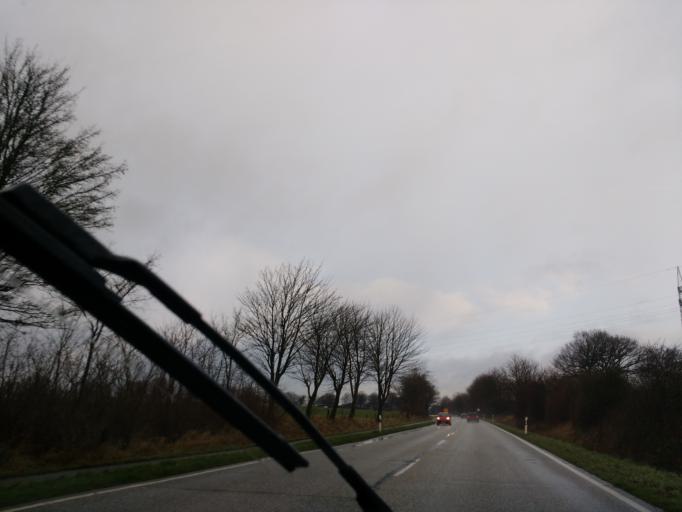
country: DE
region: Schleswig-Holstein
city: Goosefeld
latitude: 54.4240
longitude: 9.8048
